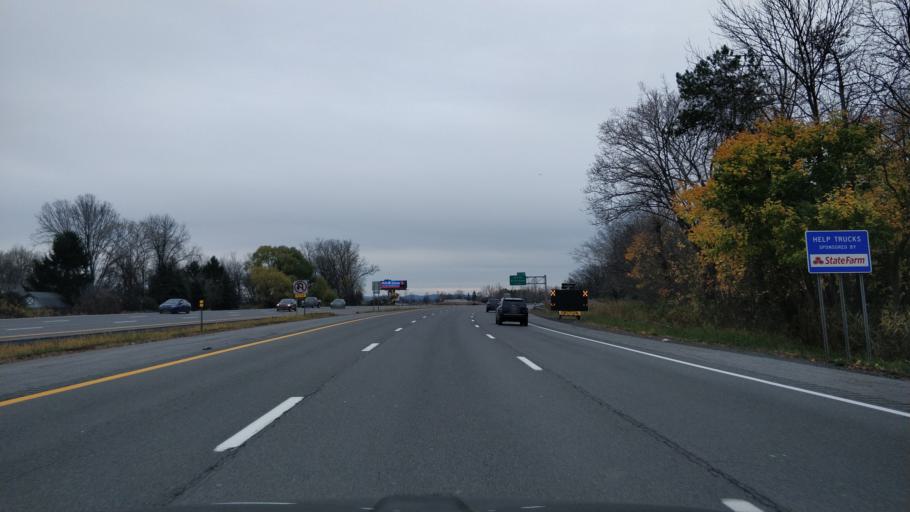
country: US
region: New York
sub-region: Onondaga County
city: North Syracuse
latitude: 43.1322
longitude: -76.1197
